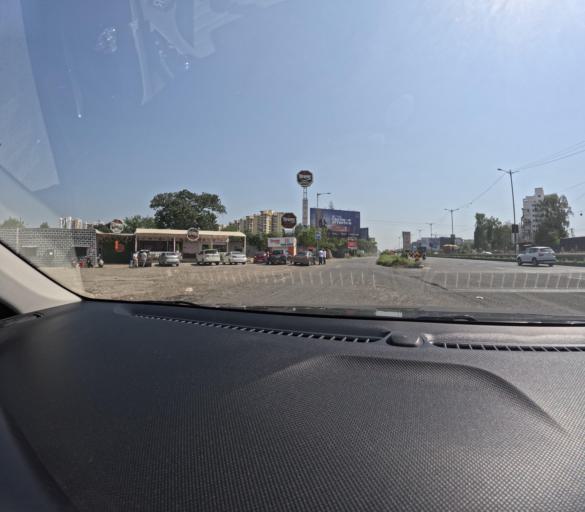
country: IN
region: Maharashtra
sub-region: Pune Division
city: Pimpri
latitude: 18.6358
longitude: 73.7397
